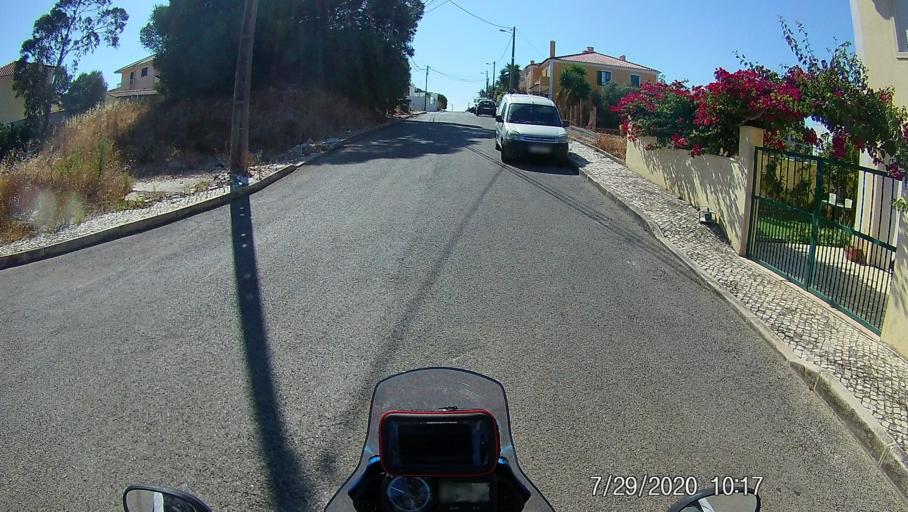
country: PT
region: Lisbon
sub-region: Cascais
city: Estoril
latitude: 38.7230
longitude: -9.3737
